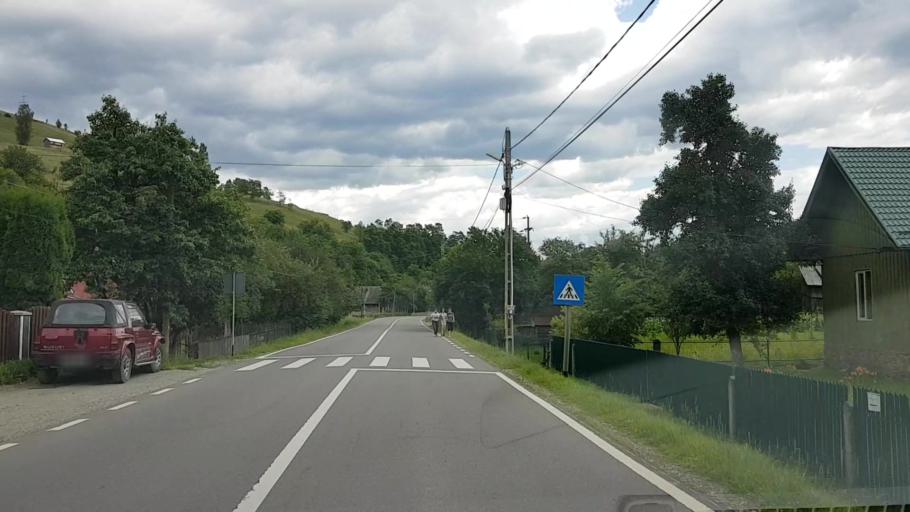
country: RO
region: Neamt
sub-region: Comuna Farcasa
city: Farcasa
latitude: 47.1615
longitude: 25.8172
